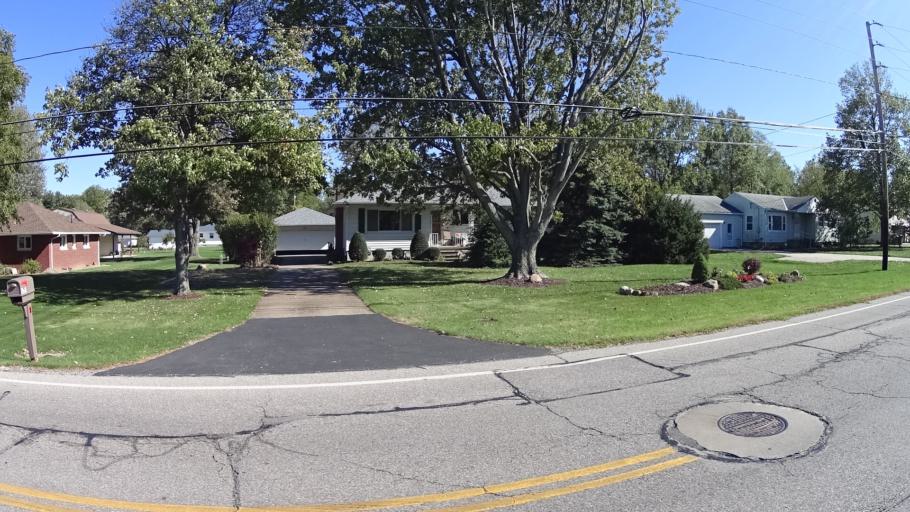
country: US
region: Ohio
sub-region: Lorain County
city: Amherst
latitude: 41.4062
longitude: -82.1837
